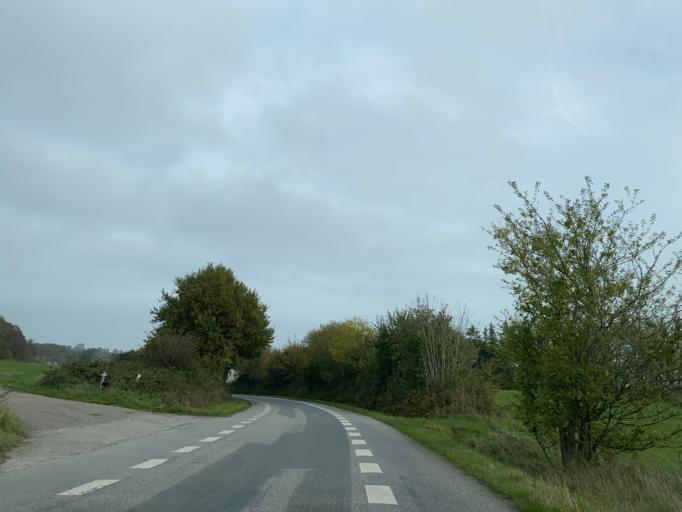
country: DK
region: South Denmark
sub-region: Aabenraa Kommune
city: Lojt Kirkeby
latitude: 55.1282
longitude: 9.4677
